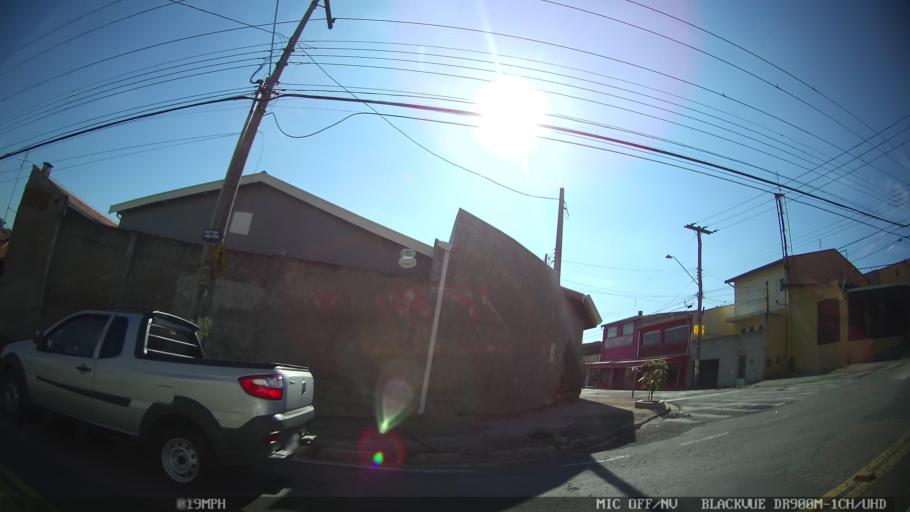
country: BR
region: Sao Paulo
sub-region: Campinas
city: Campinas
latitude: -22.9437
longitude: -47.1219
